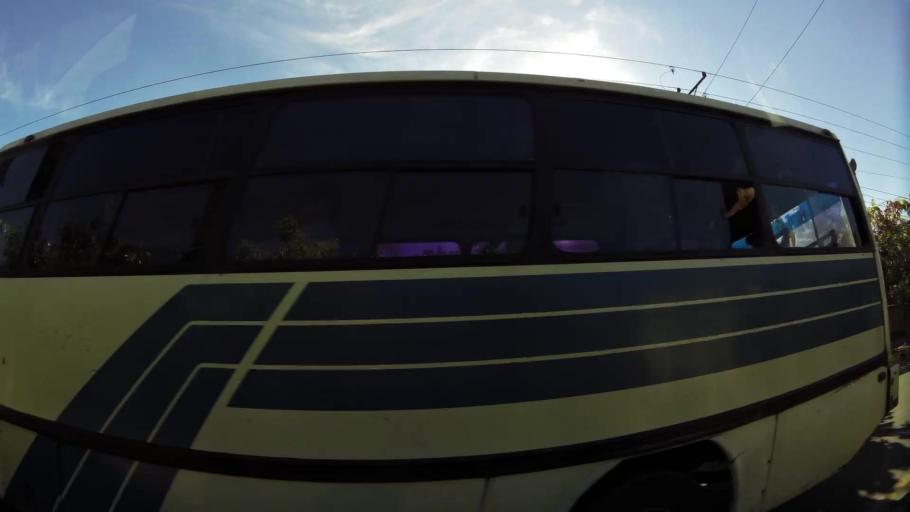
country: SV
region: Santa Ana
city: Santa Ana
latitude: 13.9705
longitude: -89.5727
